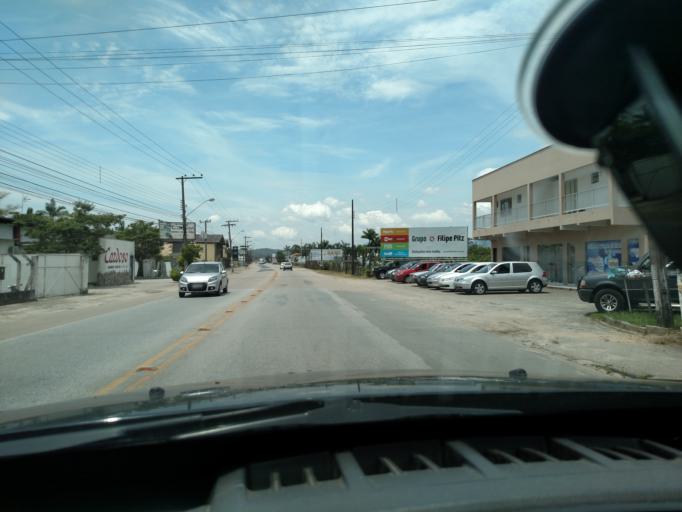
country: BR
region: Santa Catarina
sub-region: Gaspar
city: Gaspar
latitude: -26.9093
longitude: -48.9852
